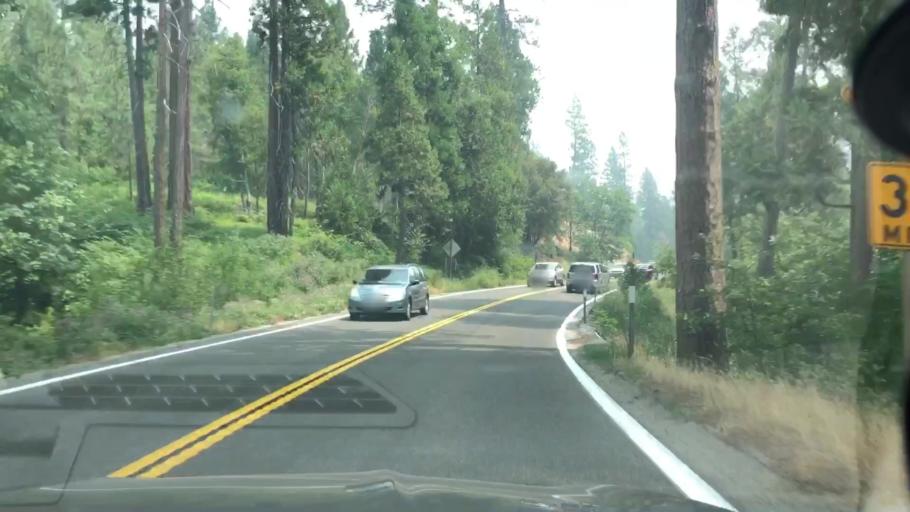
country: US
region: California
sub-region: El Dorado County
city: Pollock Pines
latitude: 38.7704
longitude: -120.4347
